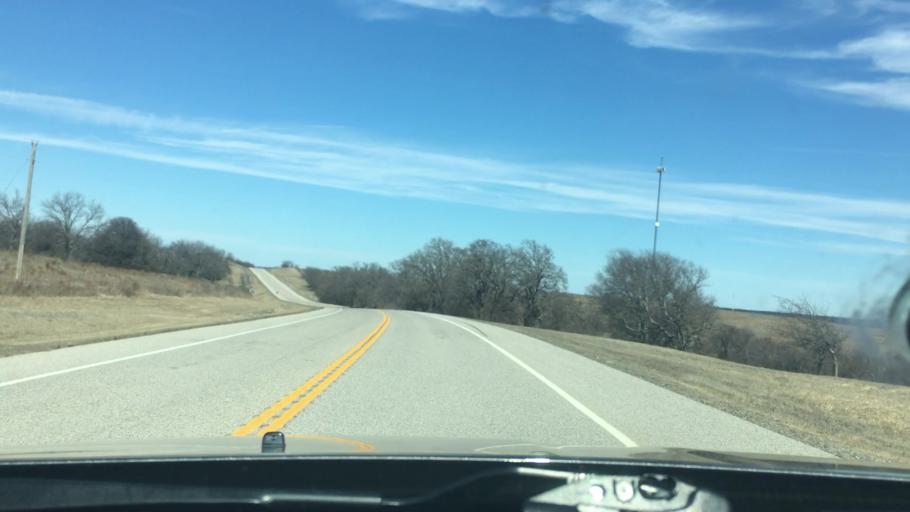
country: US
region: Oklahoma
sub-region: Carter County
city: Dickson
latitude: 34.3347
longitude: -96.9510
